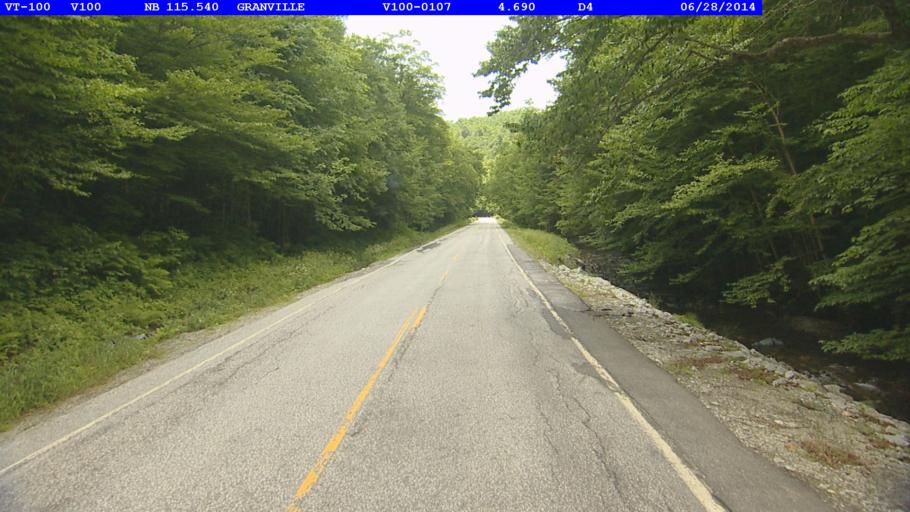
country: US
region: Vermont
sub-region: Orange County
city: Randolph
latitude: 44.0065
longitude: -72.8486
